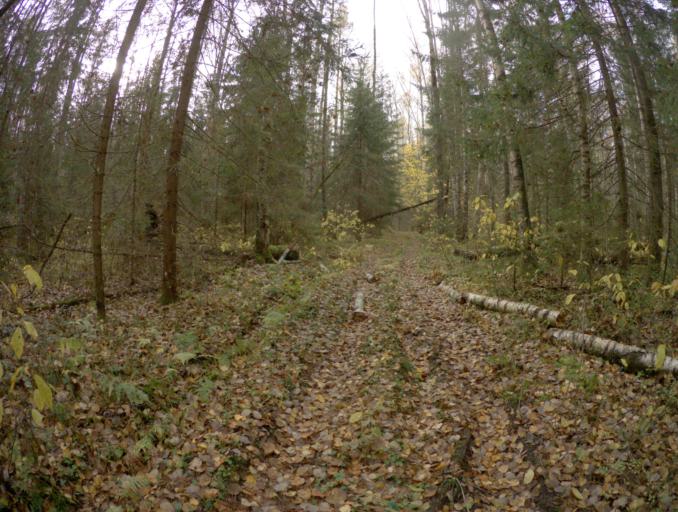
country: RU
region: Vladimir
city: Raduzhnyy
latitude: 55.9463
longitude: 40.3327
